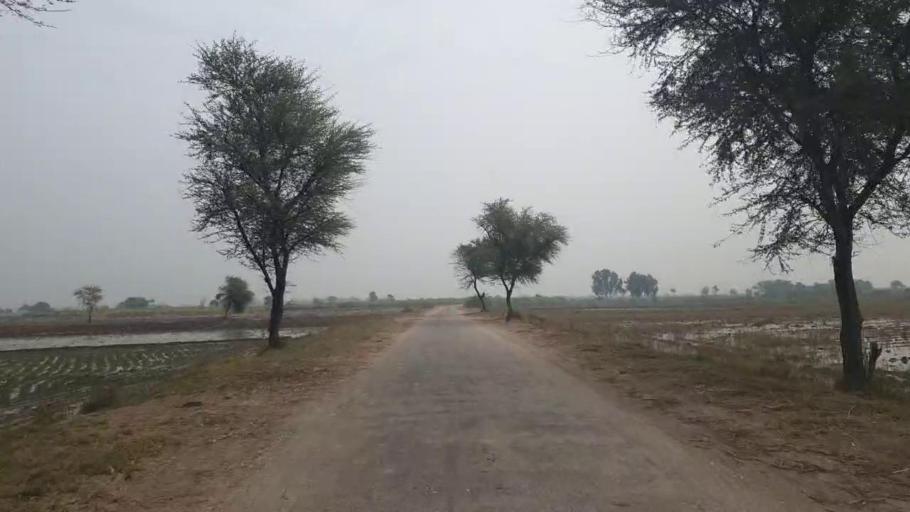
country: PK
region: Sindh
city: Tando Adam
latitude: 25.7228
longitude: 68.7111
